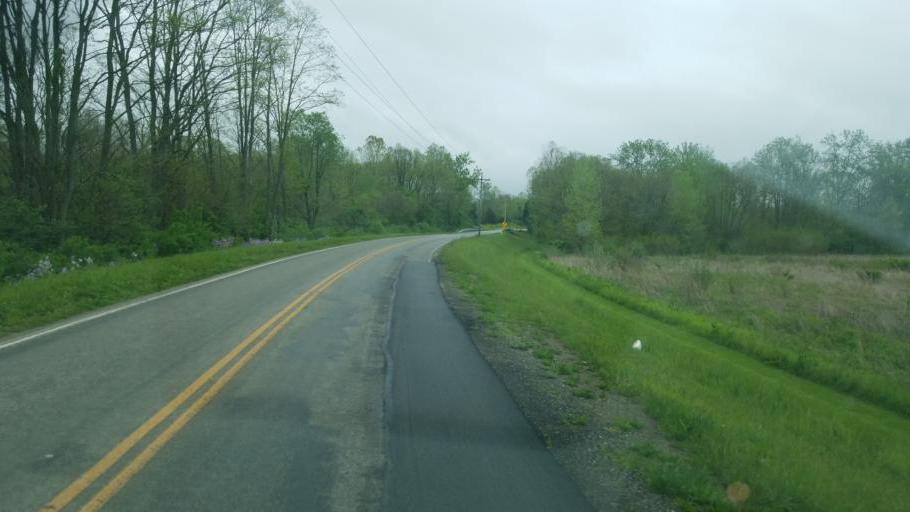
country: US
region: Ohio
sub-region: Highland County
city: Leesburg
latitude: 39.3356
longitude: -83.4695
